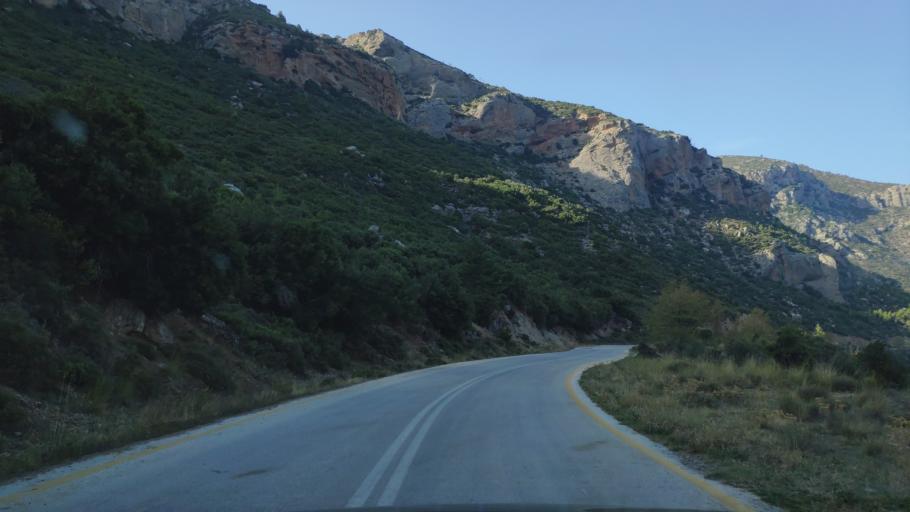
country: GR
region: West Greece
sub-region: Nomos Achaias
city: Aiyira
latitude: 38.0606
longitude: 22.3781
